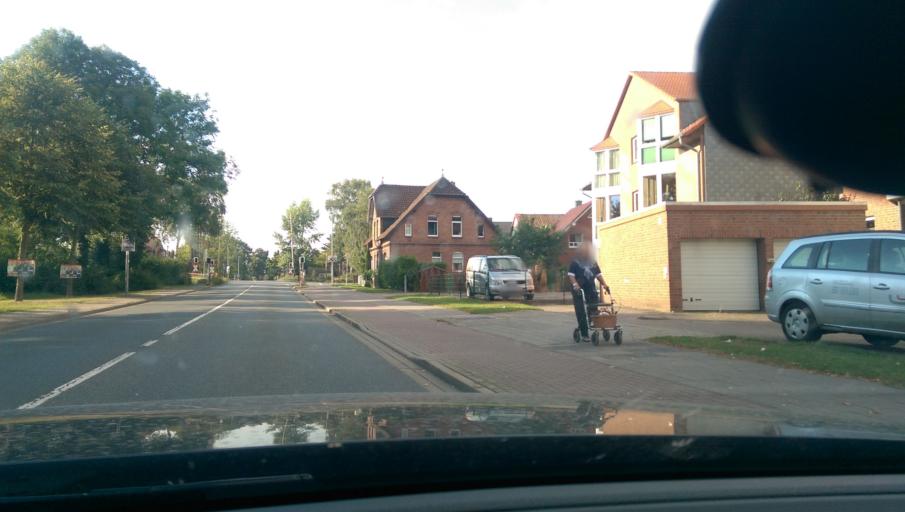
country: DE
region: Lower Saxony
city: Neustadt am Rubenberge
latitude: 52.5066
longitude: 9.4564
